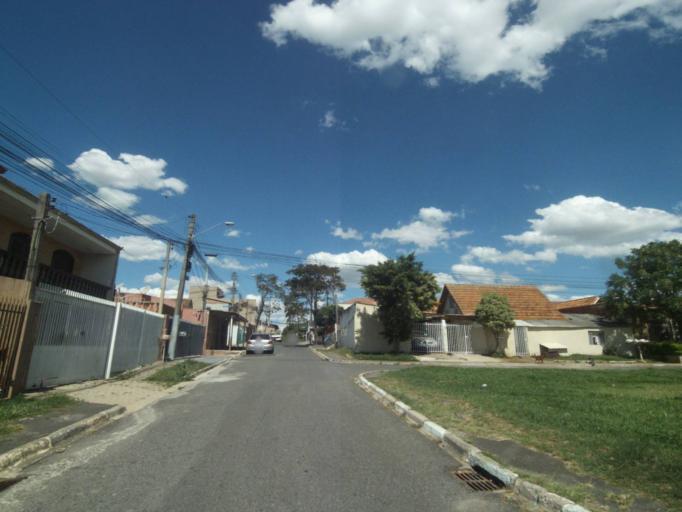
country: BR
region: Parana
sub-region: Curitiba
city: Curitiba
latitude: -25.5019
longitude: -49.3215
